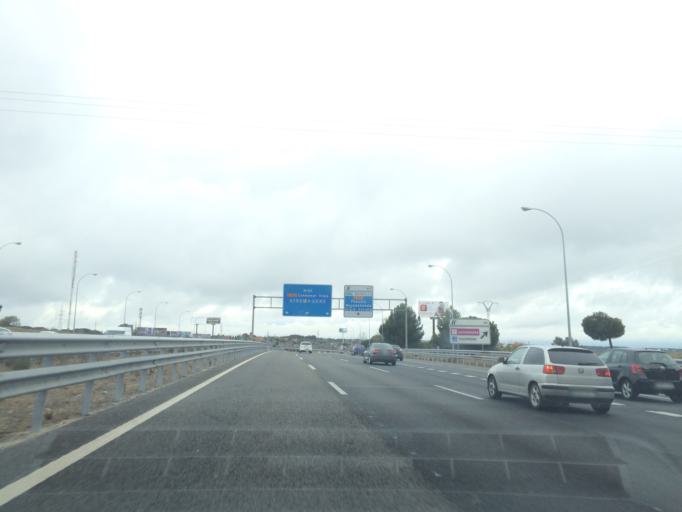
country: ES
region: Madrid
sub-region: Provincia de Madrid
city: Pozuelo de Alarcon
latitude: 40.4213
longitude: -3.8305
